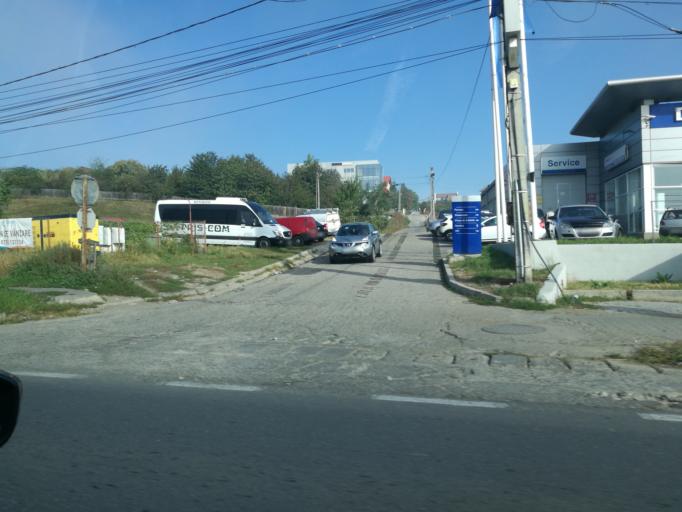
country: RO
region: Iasi
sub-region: Comuna Valea Lupului
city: Valea Lupului
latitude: 47.1724
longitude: 27.5173
